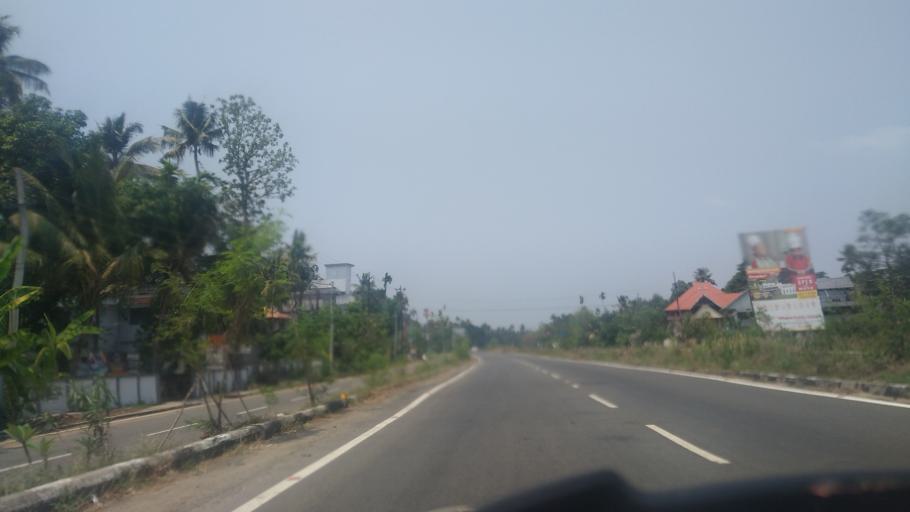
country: IN
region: Kerala
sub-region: Thrissur District
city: Kodungallur
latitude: 10.2149
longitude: 76.1974
